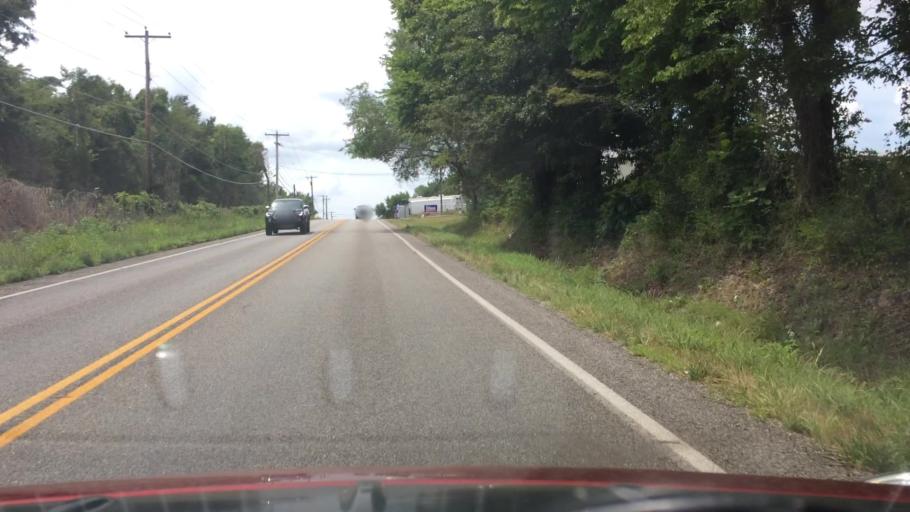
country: US
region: Missouri
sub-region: Greene County
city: Springfield
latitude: 37.2720
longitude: -93.2646
